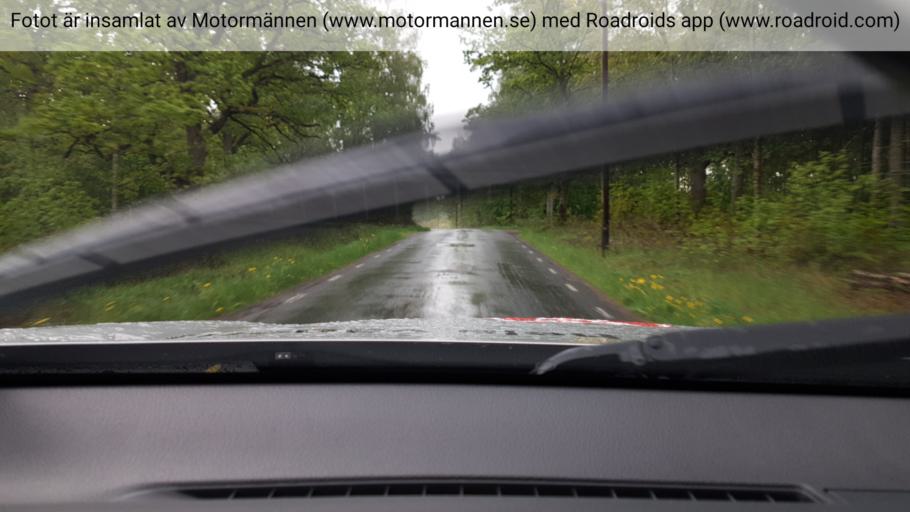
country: SE
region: Vaestra Goetaland
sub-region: Skara Kommun
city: Skara
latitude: 58.3796
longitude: 13.4690
